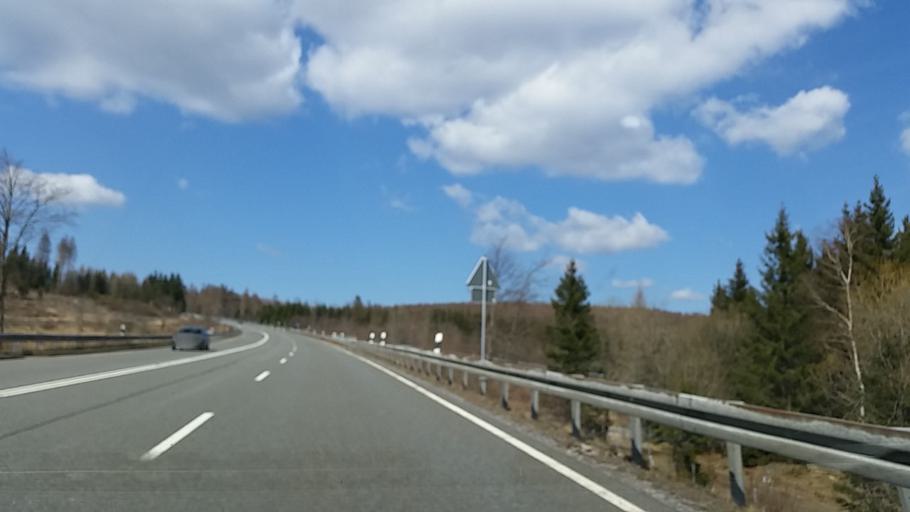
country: DE
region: Lower Saxony
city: Braunlage
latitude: 51.7386
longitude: 10.5896
